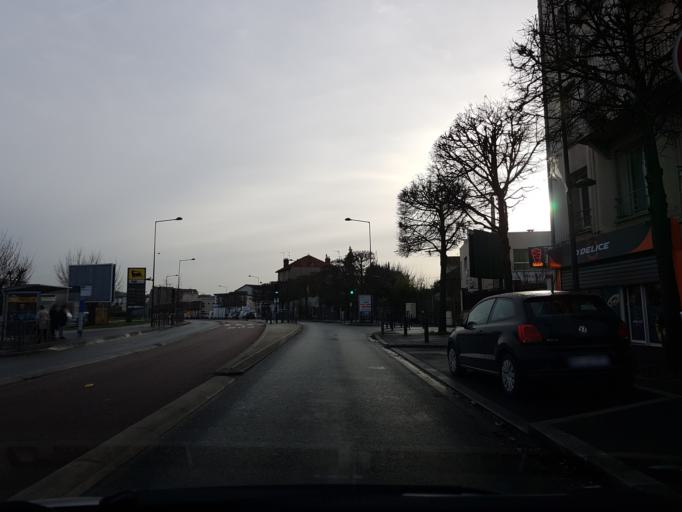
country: FR
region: Ile-de-France
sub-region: Departement du Val-de-Marne
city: Ablon-sur-Seine
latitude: 48.7288
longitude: 2.4303
